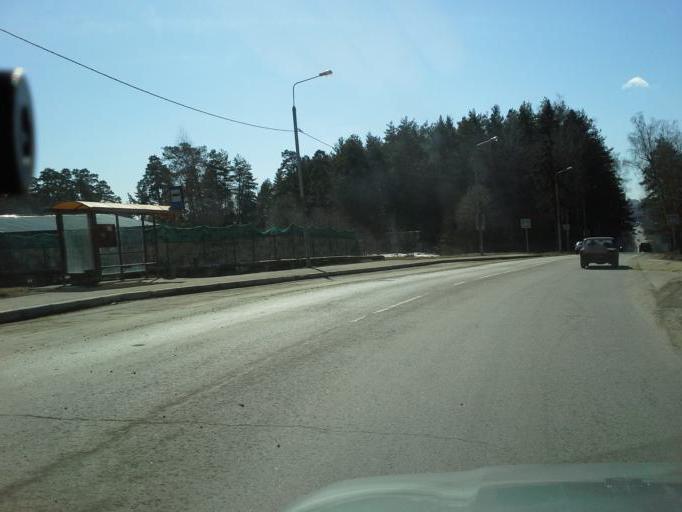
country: RU
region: Moskovskaya
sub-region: Leninskiy Rayon
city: Vnukovo
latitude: 55.6325
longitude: 37.2660
